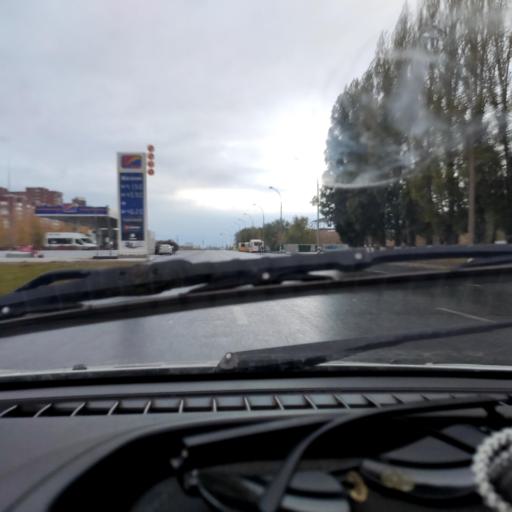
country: RU
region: Samara
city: Tol'yatti
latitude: 53.5052
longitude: 49.2755
